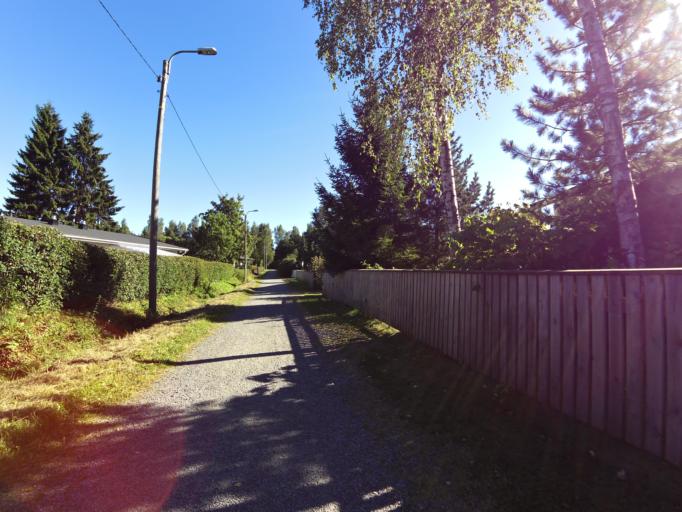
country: FI
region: Pirkanmaa
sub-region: Tampere
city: Yloejaervi
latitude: 61.5097
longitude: 23.6028
